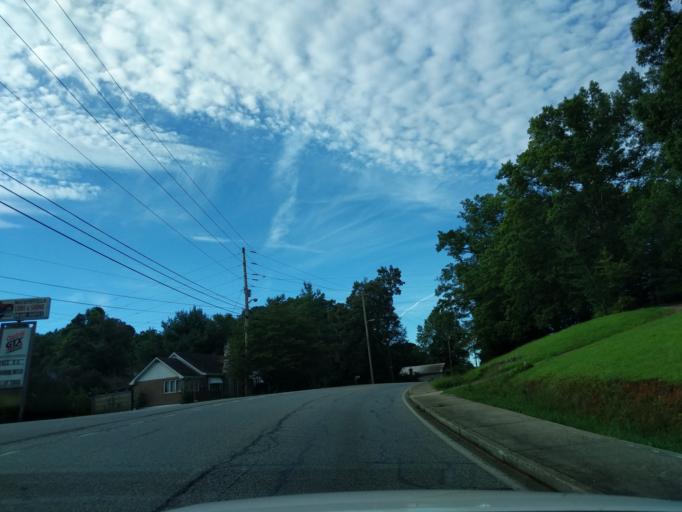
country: US
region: Georgia
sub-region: Fannin County
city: McCaysville
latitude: 34.9745
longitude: -84.3708
